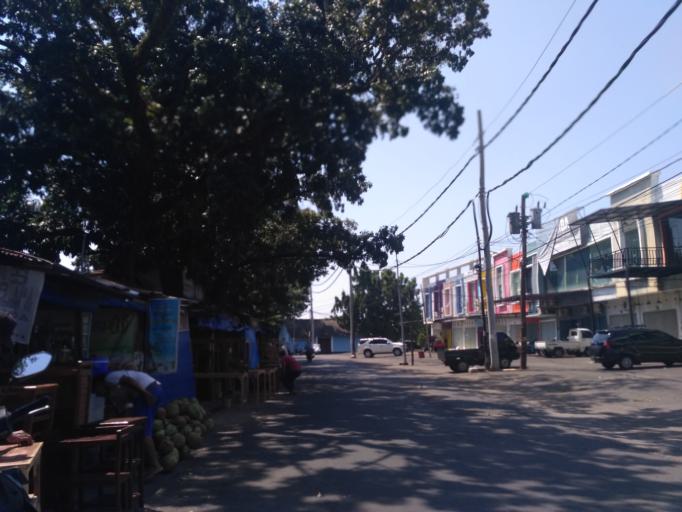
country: ID
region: Central Java
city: Semarang
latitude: -7.0010
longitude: 110.4371
